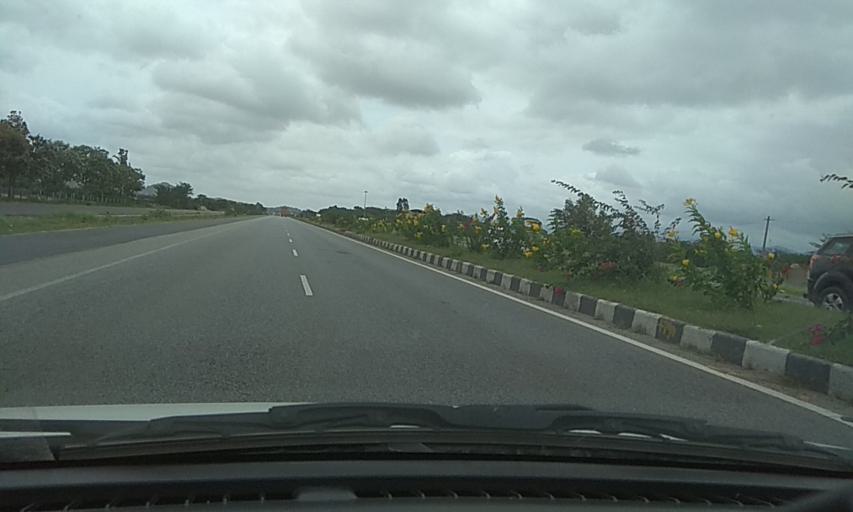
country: IN
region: Karnataka
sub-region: Chitradurga
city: Chitradurga
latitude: 14.2712
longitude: 76.3268
